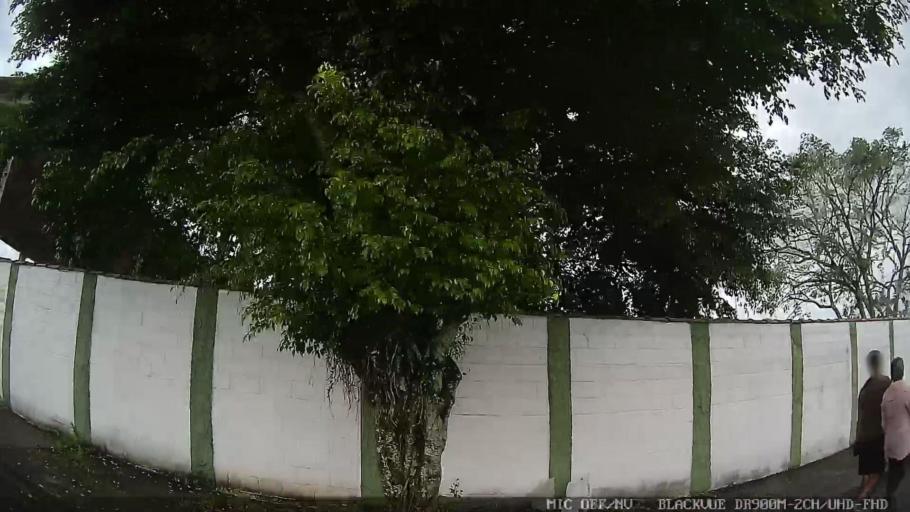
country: BR
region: Sao Paulo
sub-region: Itanhaem
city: Itanhaem
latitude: -24.1881
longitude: -46.8143
